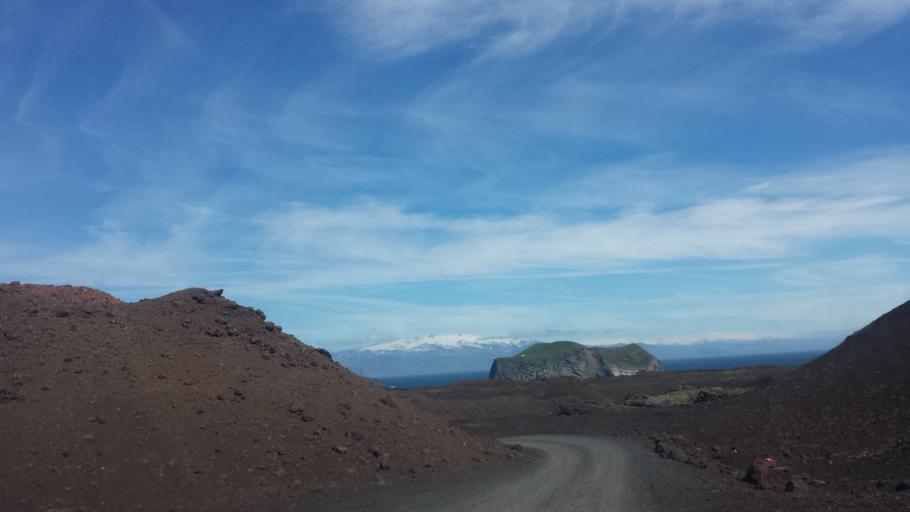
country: IS
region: South
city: Vestmannaeyjar
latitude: 63.4349
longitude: -20.2498
